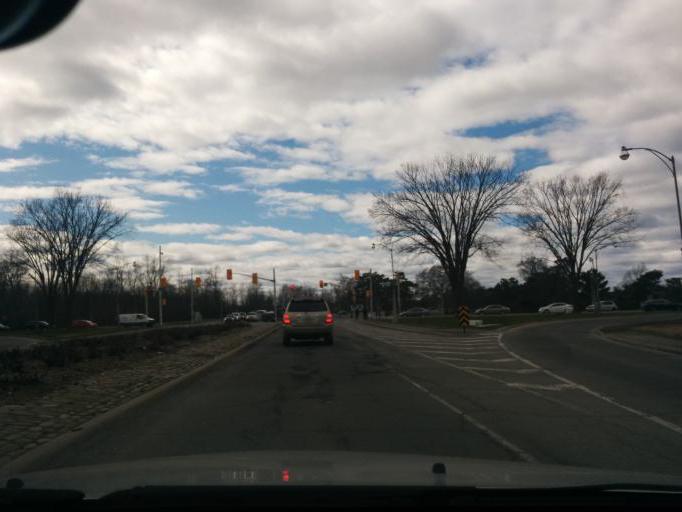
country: CA
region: Ontario
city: Ottawa
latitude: 45.4023
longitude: -75.7517
